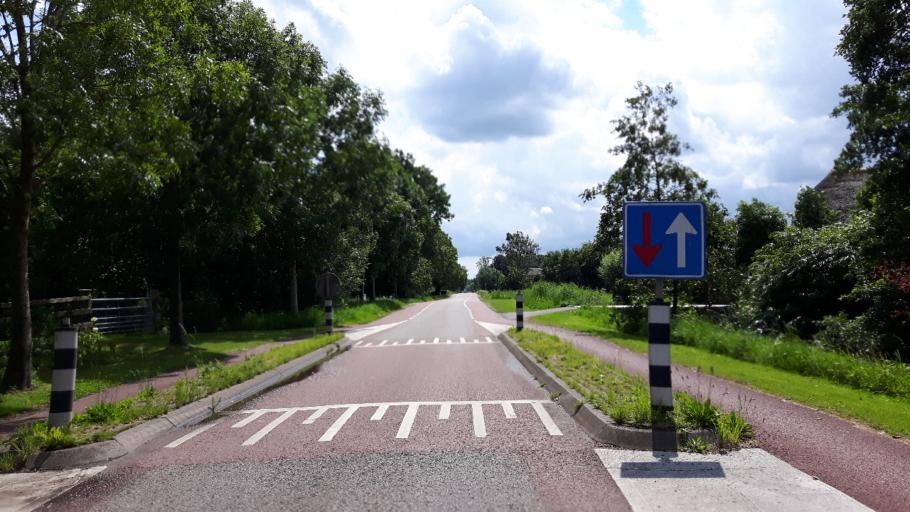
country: NL
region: Utrecht
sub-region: Stichtse Vecht
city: Breukelen
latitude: 52.1748
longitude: 4.9425
